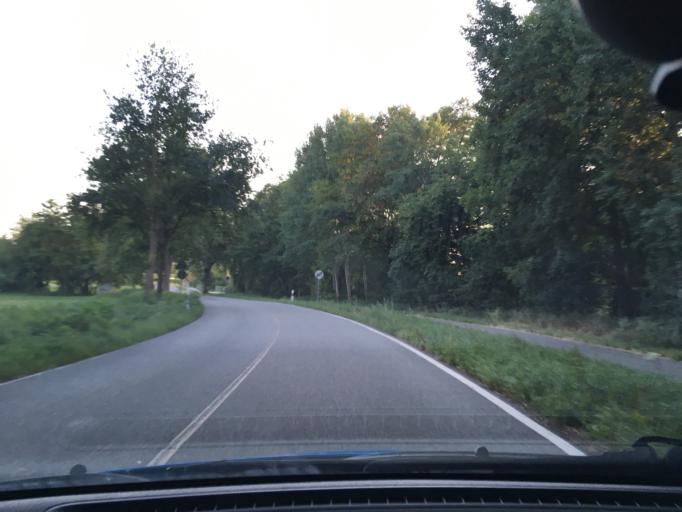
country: DE
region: Mecklenburg-Vorpommern
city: Boizenburg
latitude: 53.3935
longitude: 10.7383
